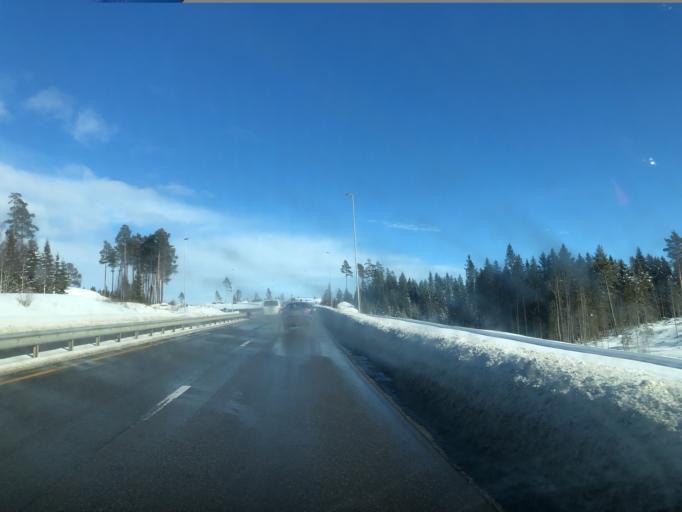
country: NO
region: Oppland
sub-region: Gran
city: Jaren
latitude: 60.4337
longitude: 10.5876
